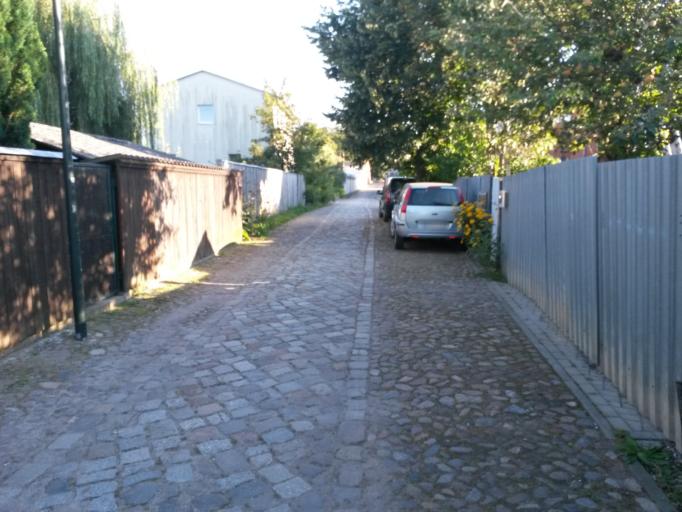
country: DE
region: Brandenburg
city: Angermunde
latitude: 53.0180
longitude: 14.0084
